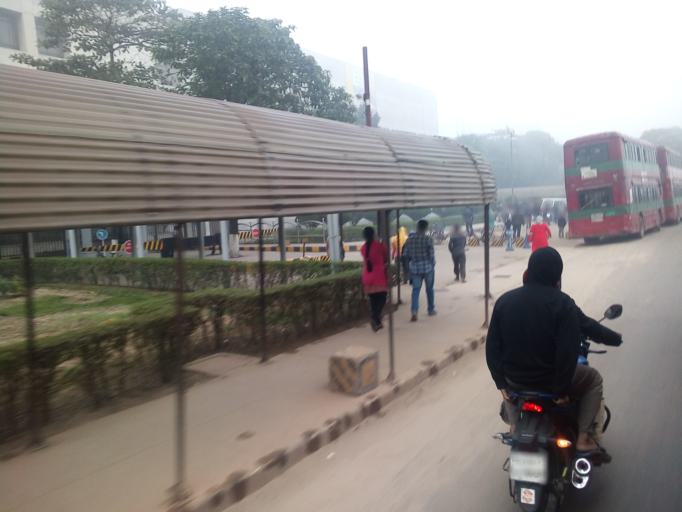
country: BD
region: Dhaka
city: Azimpur
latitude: 23.7779
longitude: 90.3801
